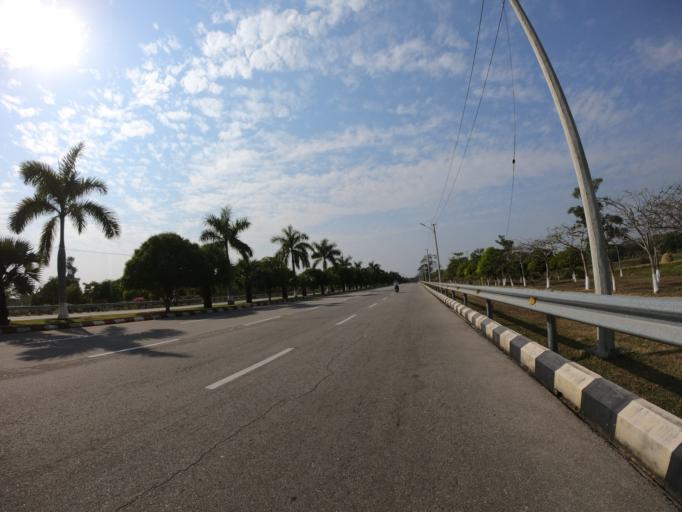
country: MM
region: Mandalay
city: Nay Pyi Taw
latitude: 19.6608
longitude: 96.1257
